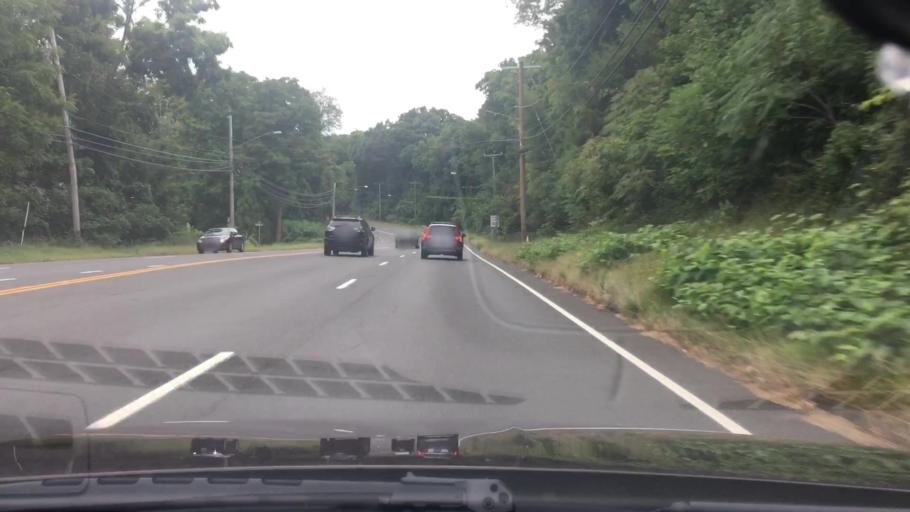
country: US
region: Connecticut
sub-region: Hartford County
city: West Hartford
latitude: 41.7879
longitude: -72.7676
